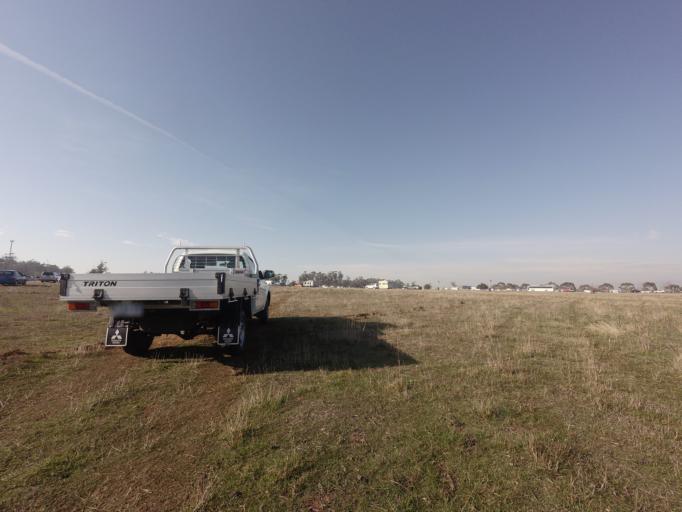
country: AU
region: Tasmania
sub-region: Northern Midlands
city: Longford
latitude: -41.5627
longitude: 146.9829
